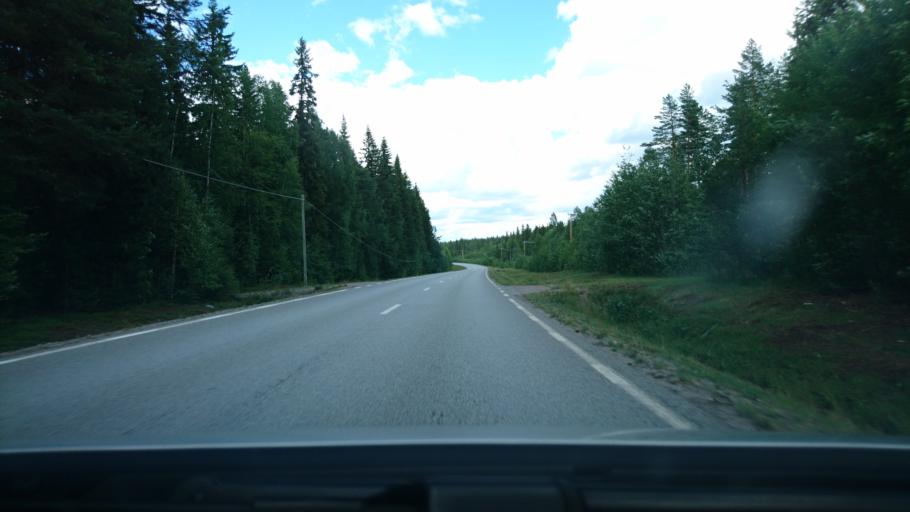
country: SE
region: Vaesternorrland
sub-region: Solleftea Kommun
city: As
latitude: 63.7028
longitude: 16.9187
